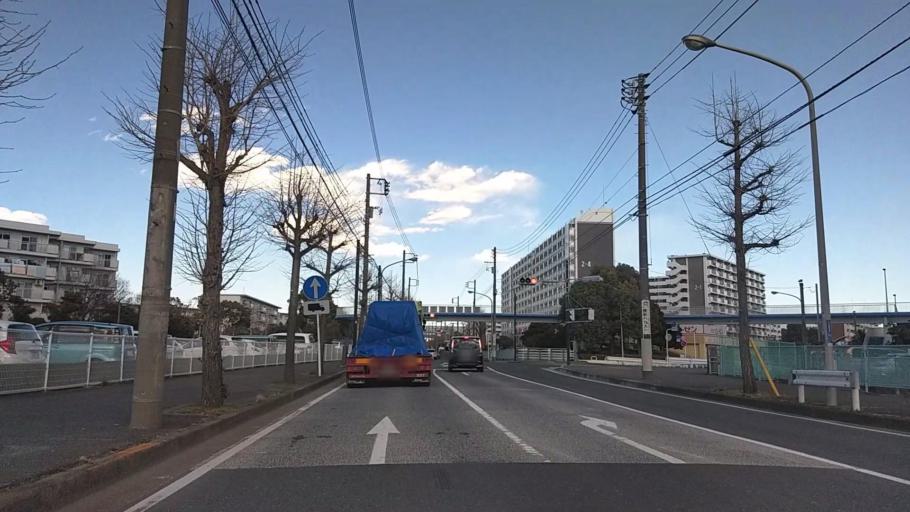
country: JP
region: Kanagawa
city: Yokohama
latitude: 35.3744
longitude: 139.6373
